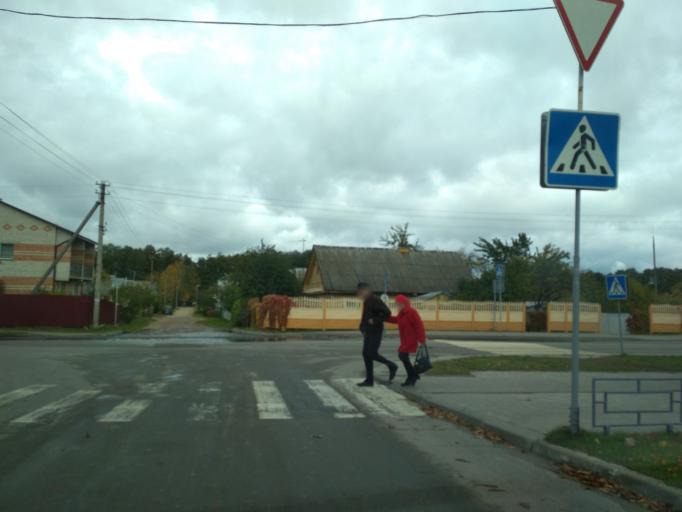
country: BY
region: Minsk
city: Mar''ina Horka
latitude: 53.5192
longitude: 28.1541
